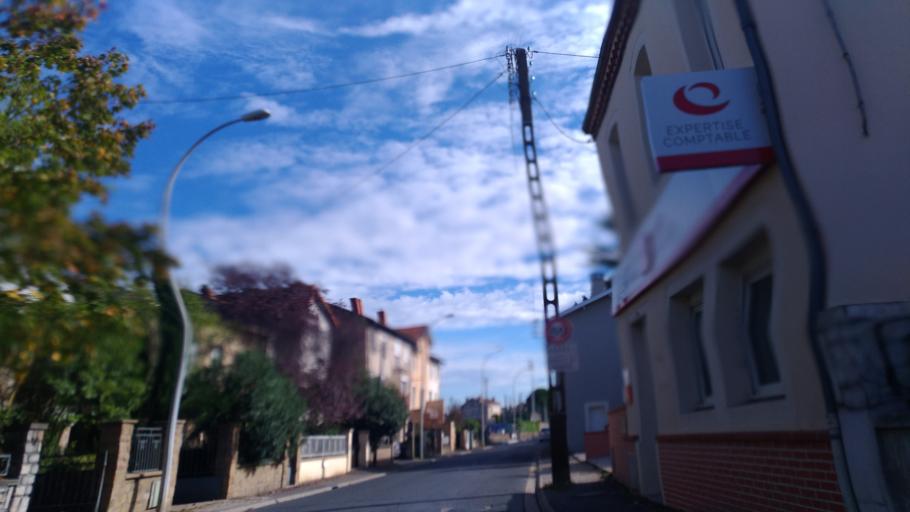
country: FR
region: Midi-Pyrenees
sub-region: Departement du Tarn
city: Albi
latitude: 43.9244
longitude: 2.1348
